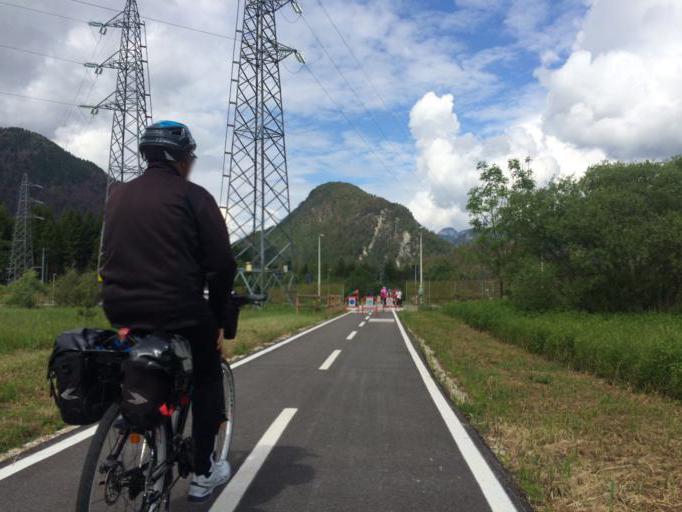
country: IT
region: Friuli Venezia Giulia
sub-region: Provincia di Udine
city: Malborghetto
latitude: 46.5010
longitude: 13.5000
